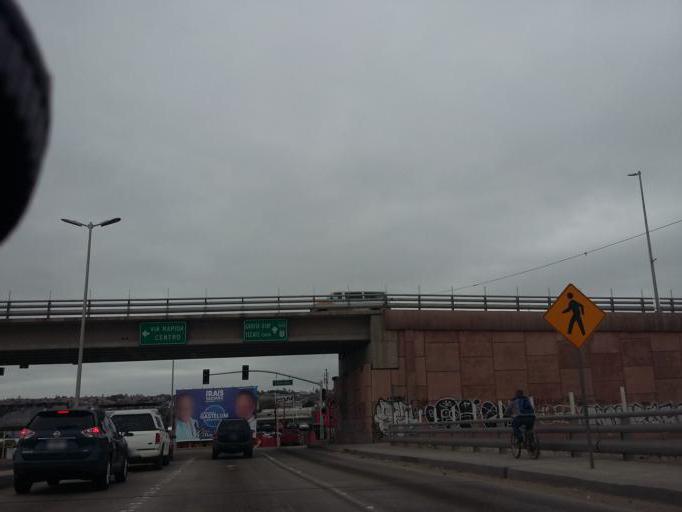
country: MX
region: Baja California
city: Tijuana
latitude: 32.5157
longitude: -116.9256
